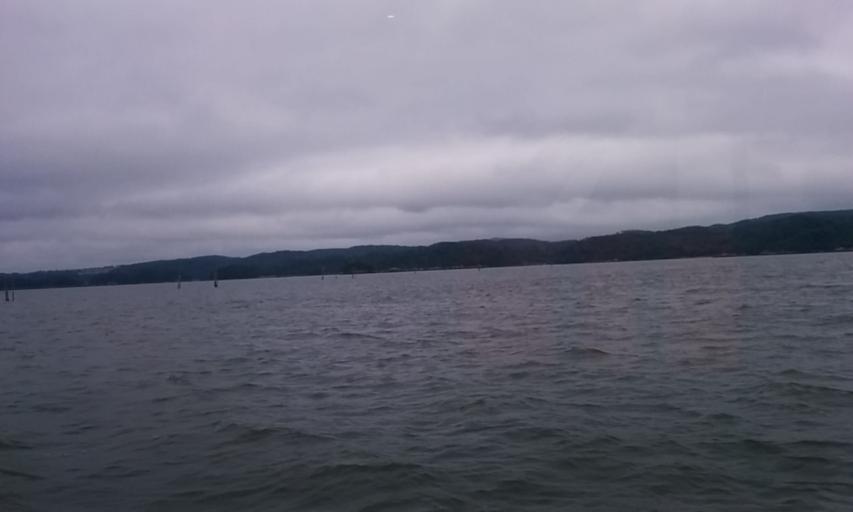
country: JP
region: Miyagi
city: Matsushima
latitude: 38.3430
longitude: 141.0746
